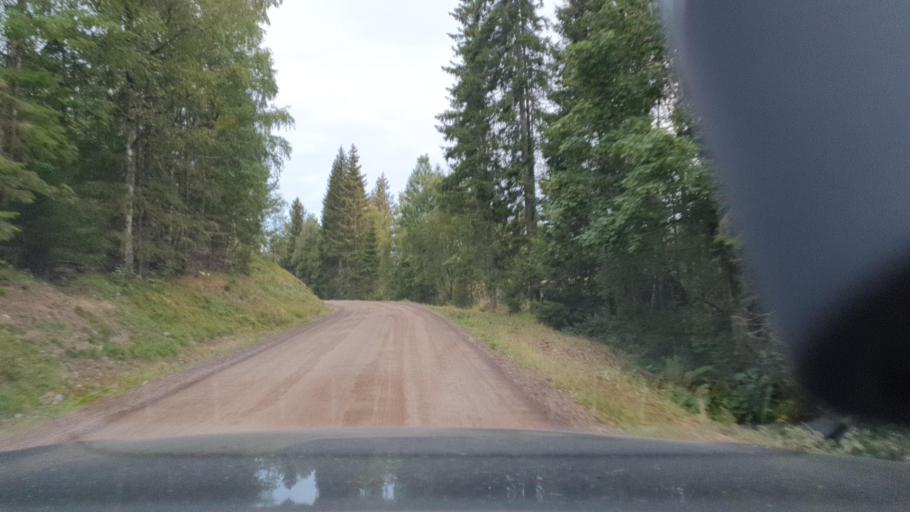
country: SE
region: Vaermland
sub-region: Sunne Kommun
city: Sunne
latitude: 59.8224
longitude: 12.8766
